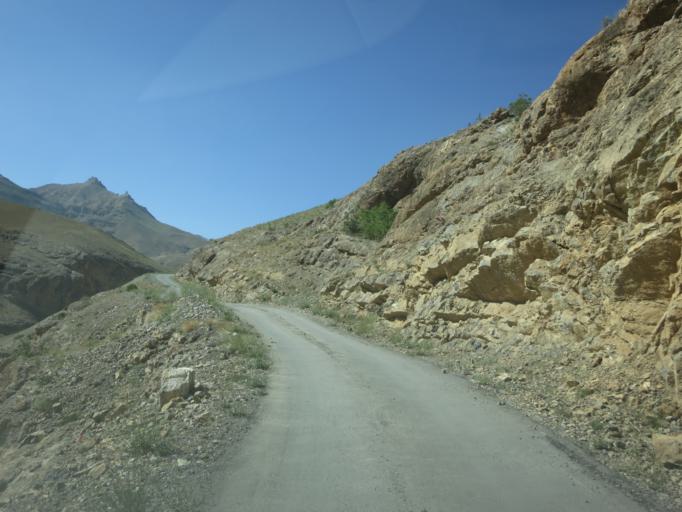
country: IN
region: Himachal Pradesh
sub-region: Kulu
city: Manali
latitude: 32.3206
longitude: 78.0017
